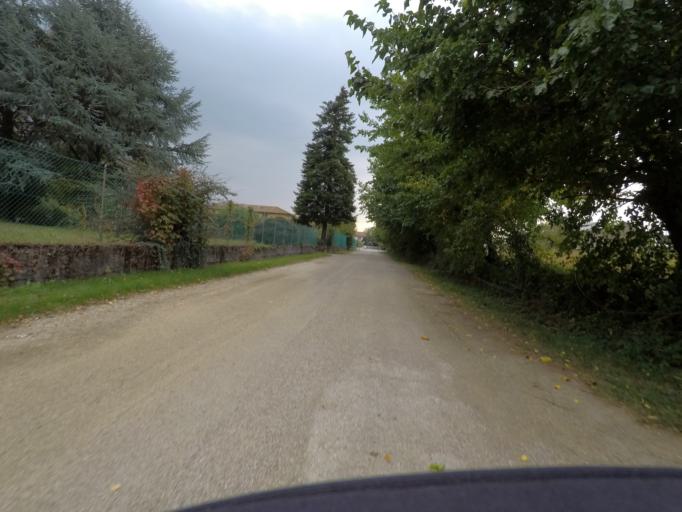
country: IT
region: Friuli Venezia Giulia
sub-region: Provincia di Udine
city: Feletto Umberto
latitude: 46.1020
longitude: 13.2402
